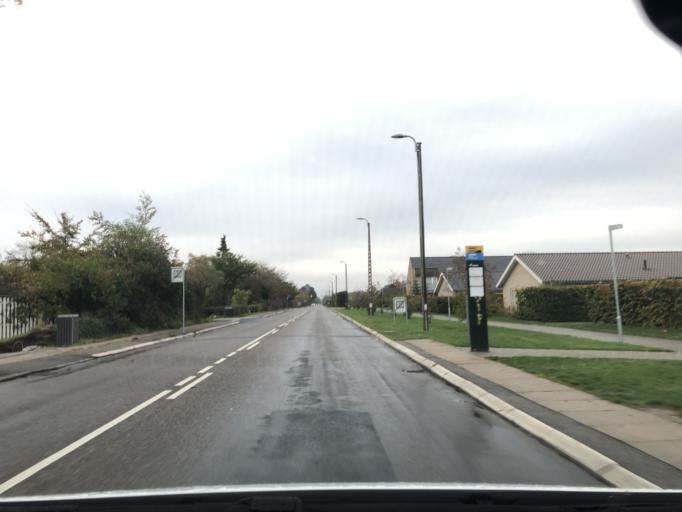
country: DK
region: Capital Region
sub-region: Dragor Kommune
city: Dragor
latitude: 55.5835
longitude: 12.6374
